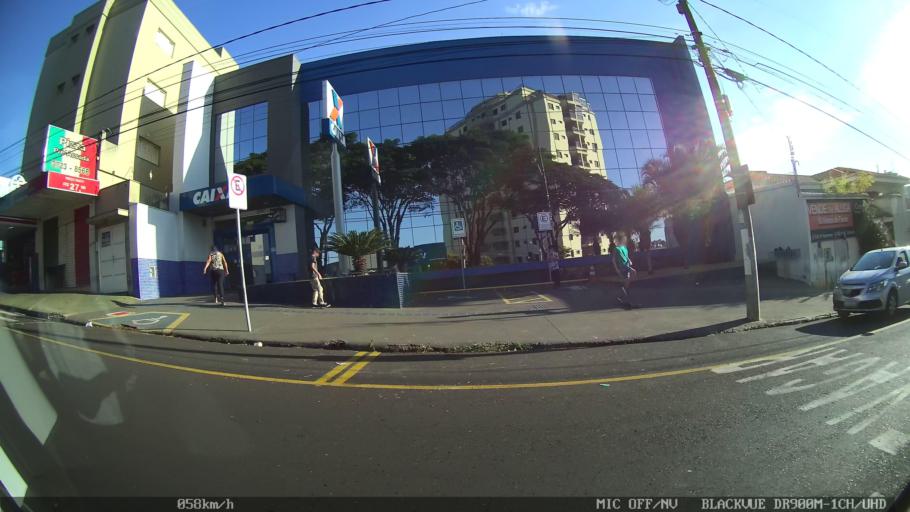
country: BR
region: Sao Paulo
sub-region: Franca
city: Franca
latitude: -20.5392
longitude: -47.3895
